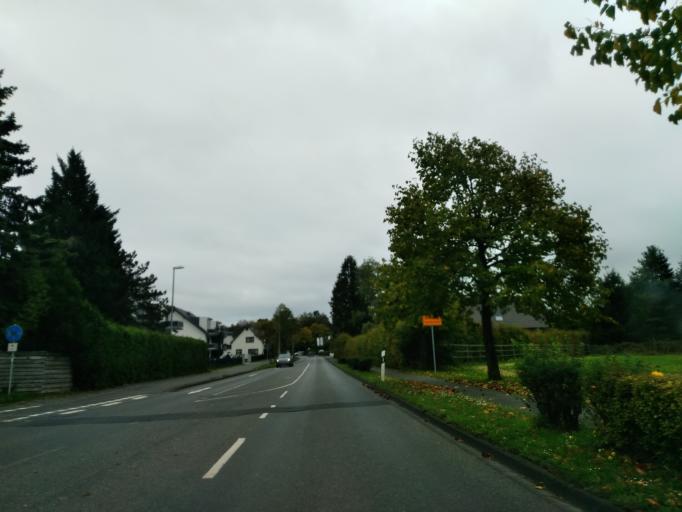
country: DE
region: Rheinland-Pfalz
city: Windhagen
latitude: 50.6558
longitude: 7.3019
